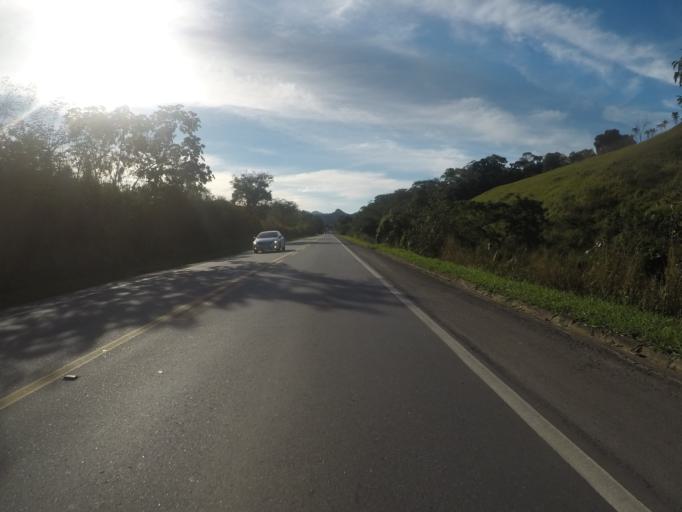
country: BR
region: Espirito Santo
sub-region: Fundao
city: Fundao
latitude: -19.8899
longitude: -40.4135
